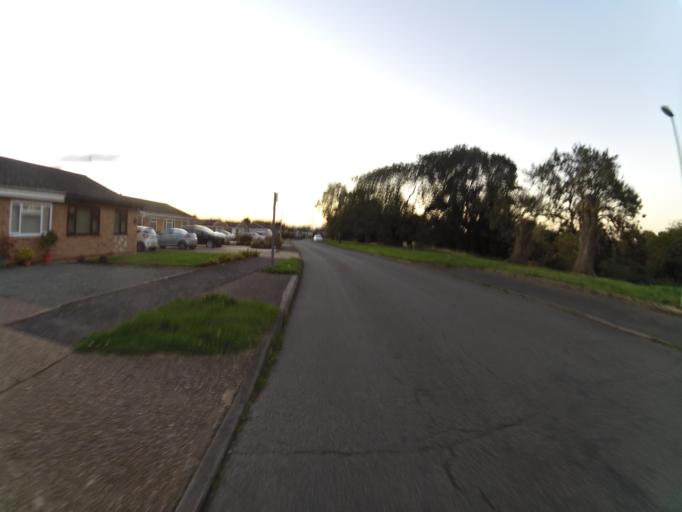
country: GB
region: England
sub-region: Suffolk
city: Bramford
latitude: 52.0801
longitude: 1.1008
